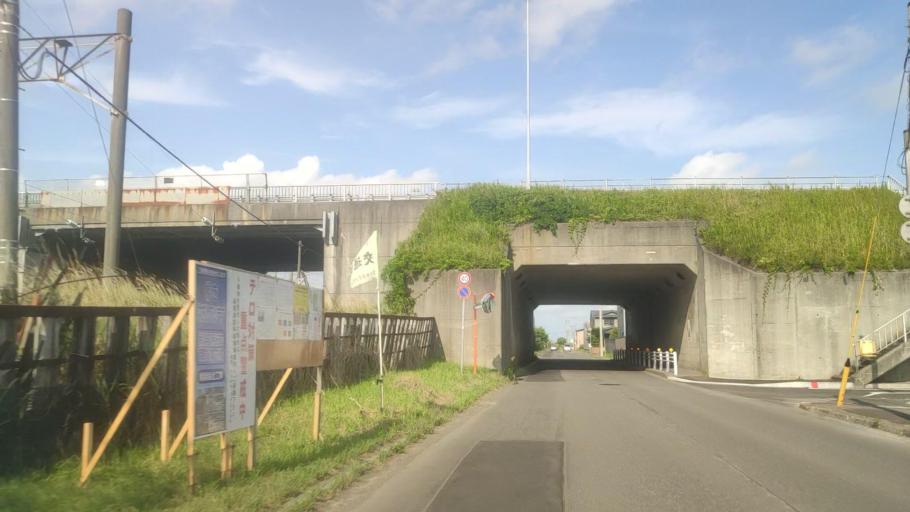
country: JP
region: Hokkaido
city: Tomakomai
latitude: 42.6465
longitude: 141.6178
